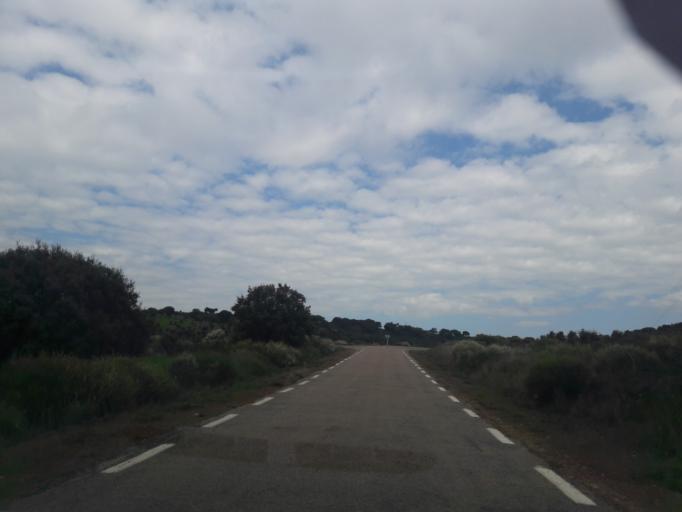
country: ES
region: Castille and Leon
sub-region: Provincia de Salamanca
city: Serradilla del Arroyo
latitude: 40.5245
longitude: -6.3813
